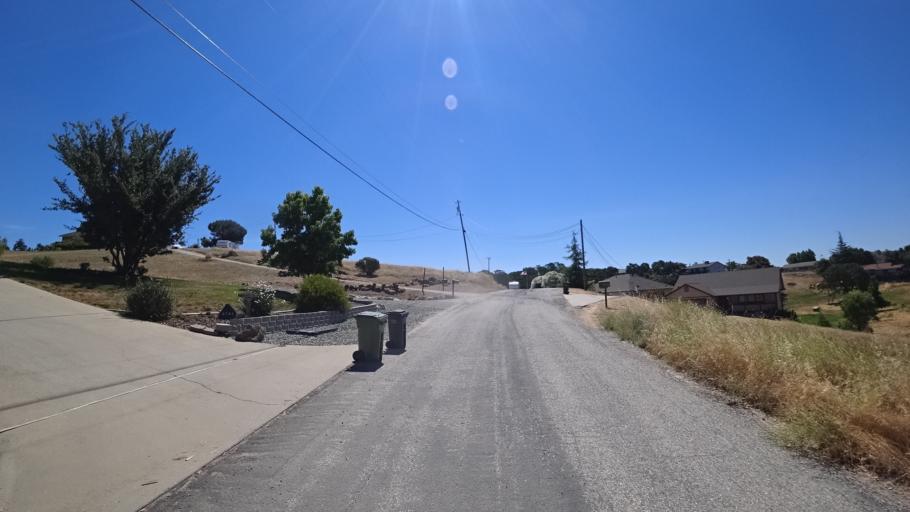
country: US
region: California
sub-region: Calaveras County
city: Valley Springs
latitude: 38.1578
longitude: -120.8326
